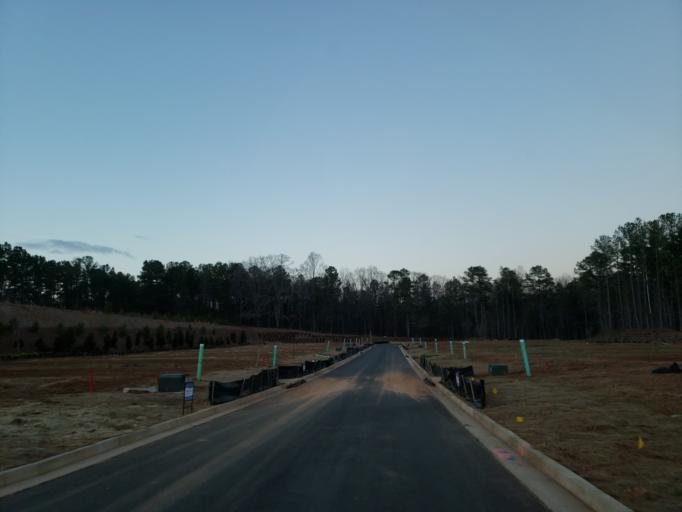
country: US
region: Georgia
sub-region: Cobb County
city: Powder Springs
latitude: 33.9344
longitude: -84.7045
